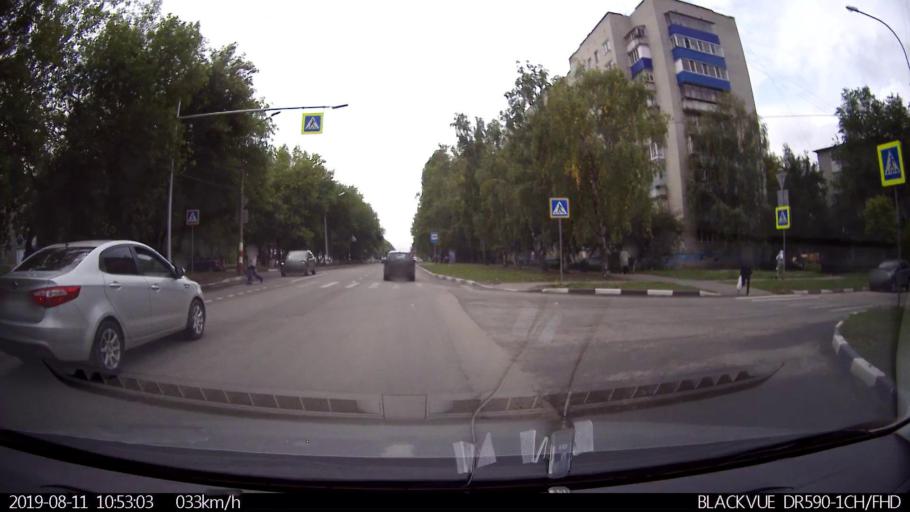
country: RU
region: Ulyanovsk
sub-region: Ulyanovskiy Rayon
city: Ulyanovsk
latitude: 54.2616
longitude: 48.3343
